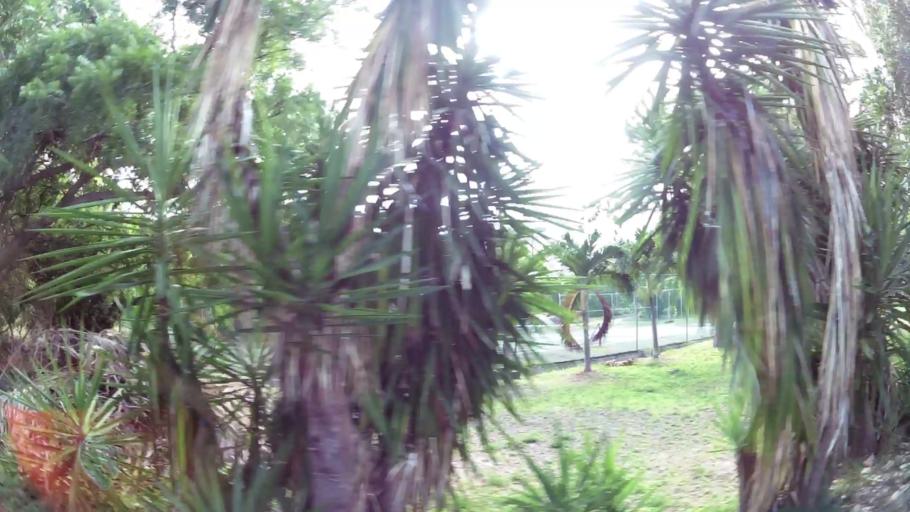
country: AG
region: Saint Peter
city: Parham
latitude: 17.0992
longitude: -61.6885
